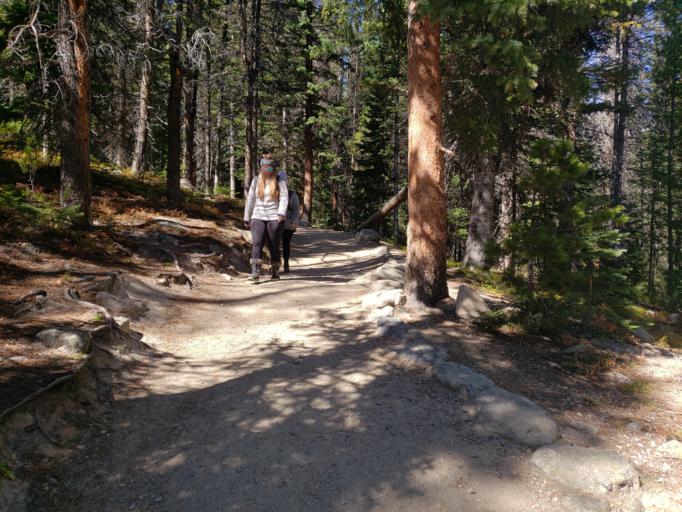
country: US
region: Colorado
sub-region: Larimer County
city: Estes Park
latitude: 40.3108
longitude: -105.6451
